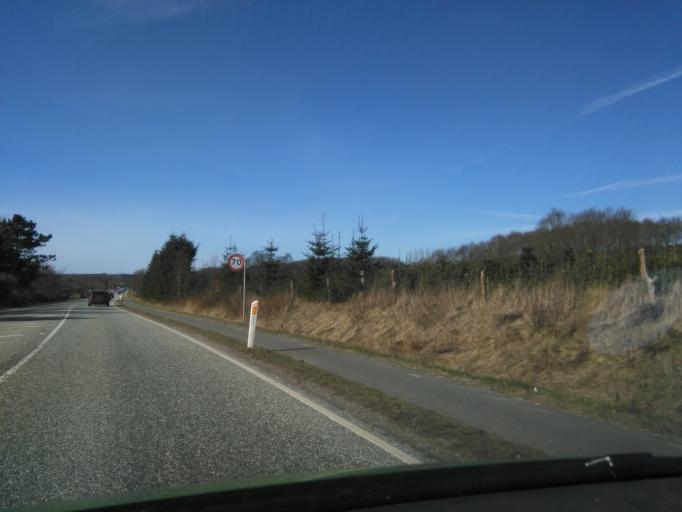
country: DK
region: Central Jutland
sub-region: Favrskov Kommune
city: Soften
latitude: 56.2407
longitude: 10.0842
